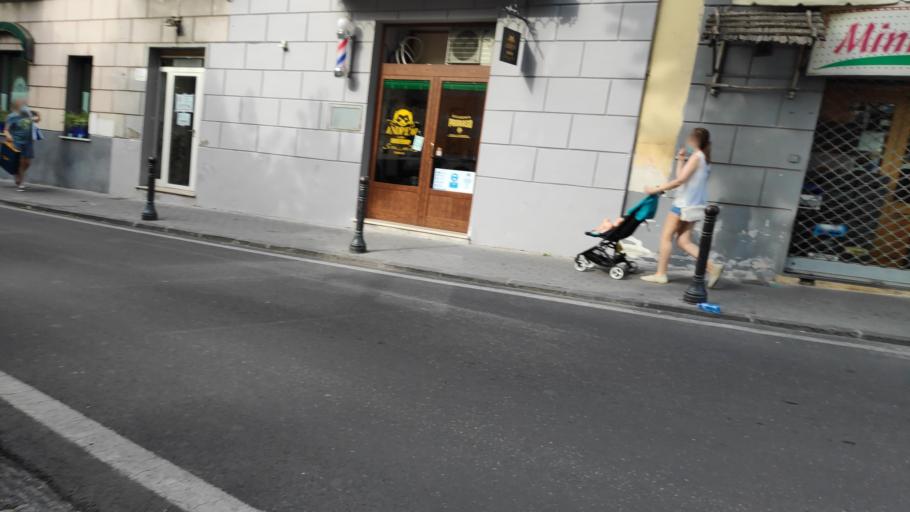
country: IT
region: Campania
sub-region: Provincia di Napoli
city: Sorrento
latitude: 40.6255
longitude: 14.3762
